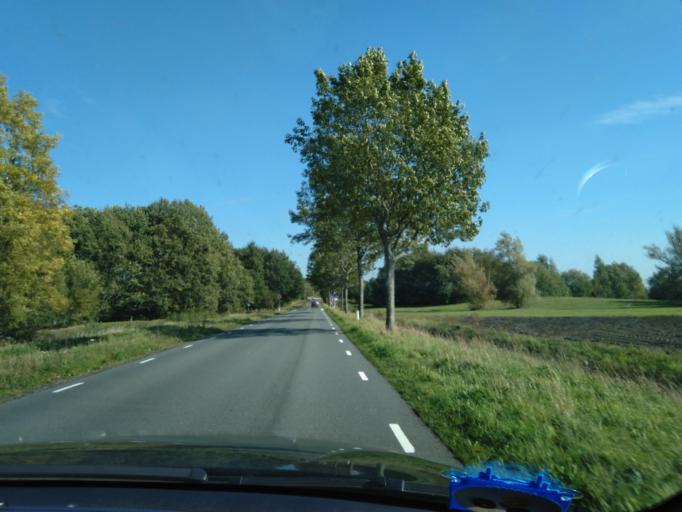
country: NL
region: Groningen
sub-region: Gemeente Veendam
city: Veendam
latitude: 53.0911
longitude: 6.8394
